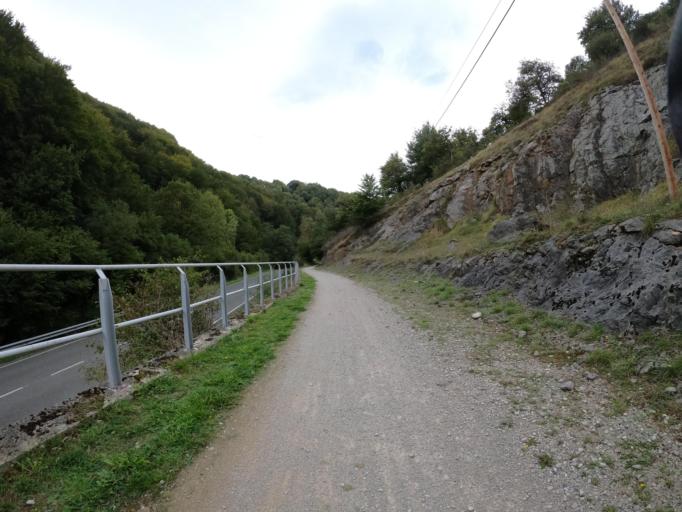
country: ES
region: Navarre
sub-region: Provincia de Navarra
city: Lekunberri
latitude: 43.0227
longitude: -1.9072
